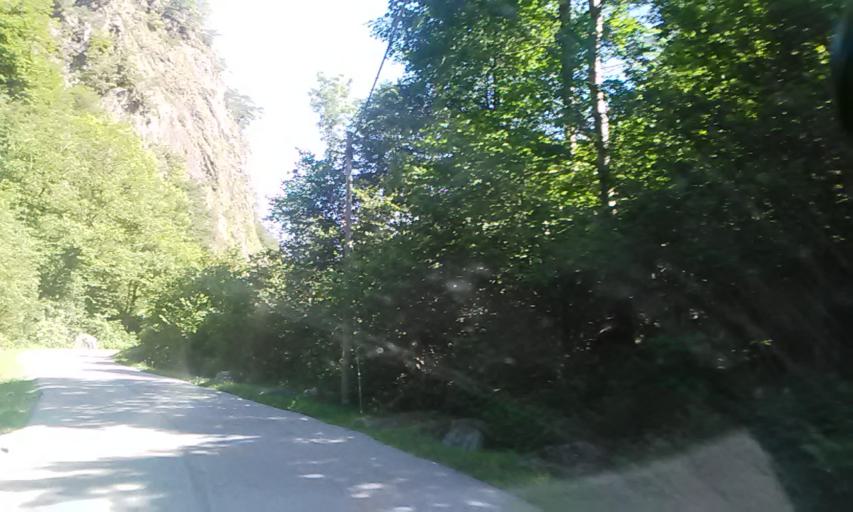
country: IT
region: Piedmont
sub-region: Provincia di Vercelli
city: Varallo
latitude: 45.8340
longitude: 8.2767
